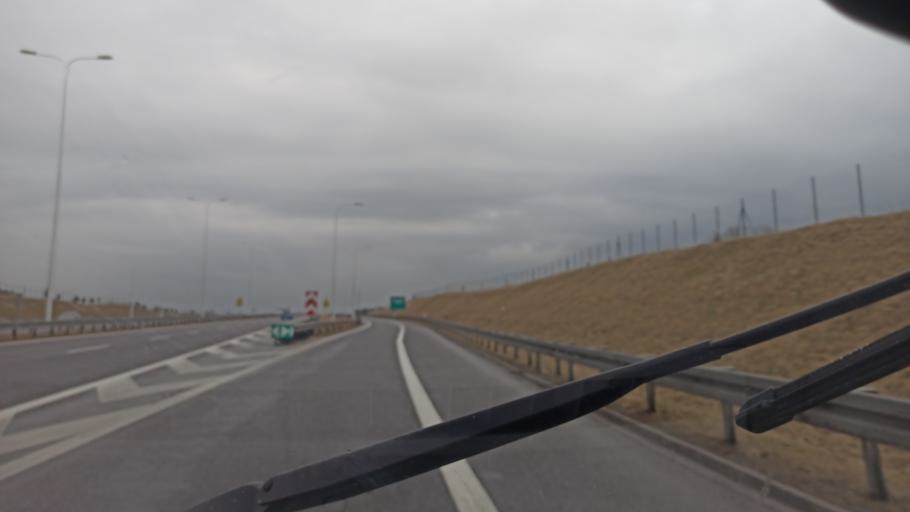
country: PL
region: Lublin Voivodeship
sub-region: Powiat lubelski
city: Jastkow
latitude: 51.2798
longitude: 22.4435
